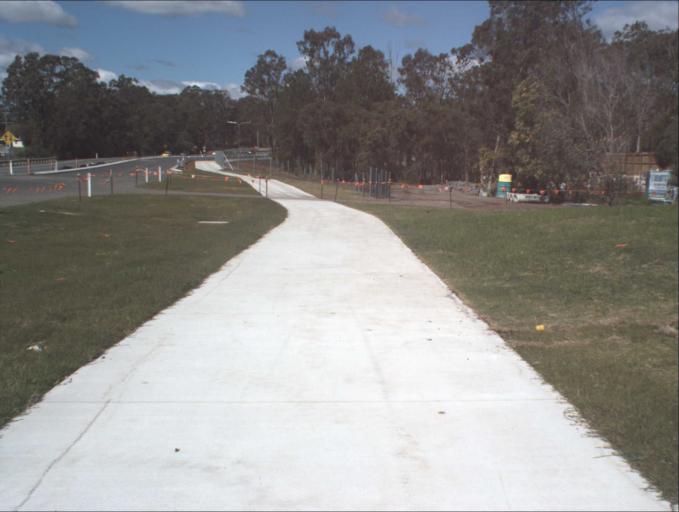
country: AU
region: Queensland
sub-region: Logan
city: Waterford West
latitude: -27.6930
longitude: 153.1022
